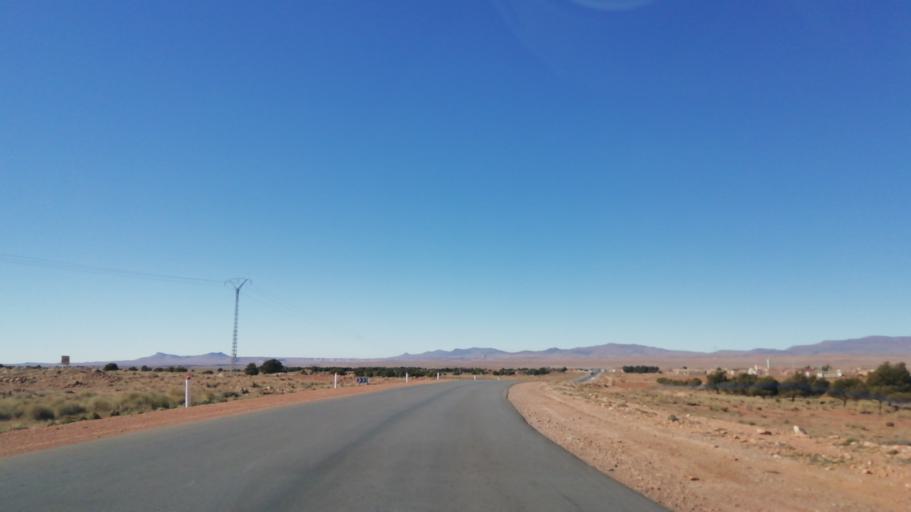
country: DZ
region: El Bayadh
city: El Bayadh
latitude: 33.6315
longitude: 1.3631
